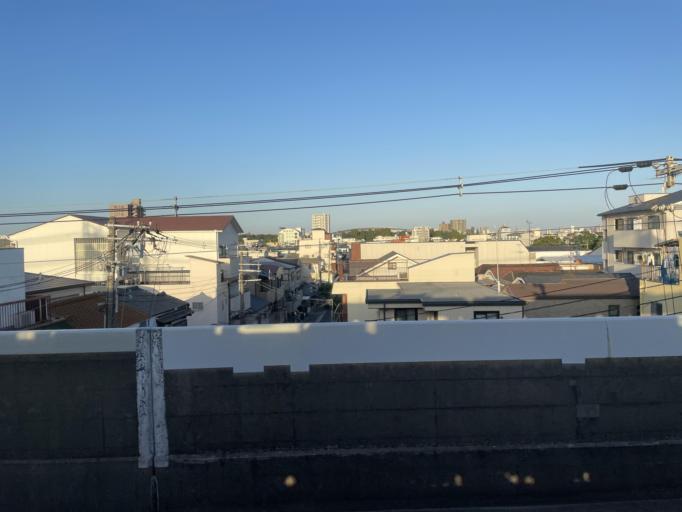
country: JP
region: Osaka
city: Matsubara
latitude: 34.6143
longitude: 135.5334
